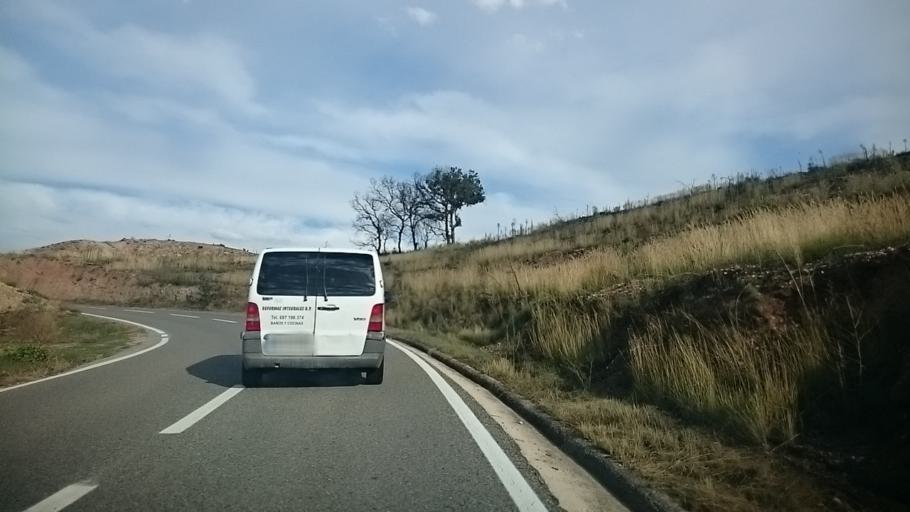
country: ES
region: Catalonia
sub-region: Provincia de Barcelona
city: Castelloli
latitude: 41.6255
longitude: 1.6831
